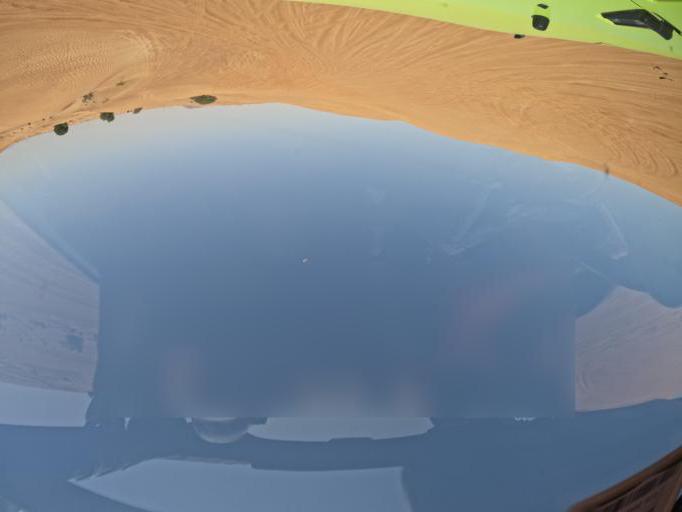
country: AE
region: Ash Shariqah
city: Adh Dhayd
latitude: 24.9886
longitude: 55.7234
